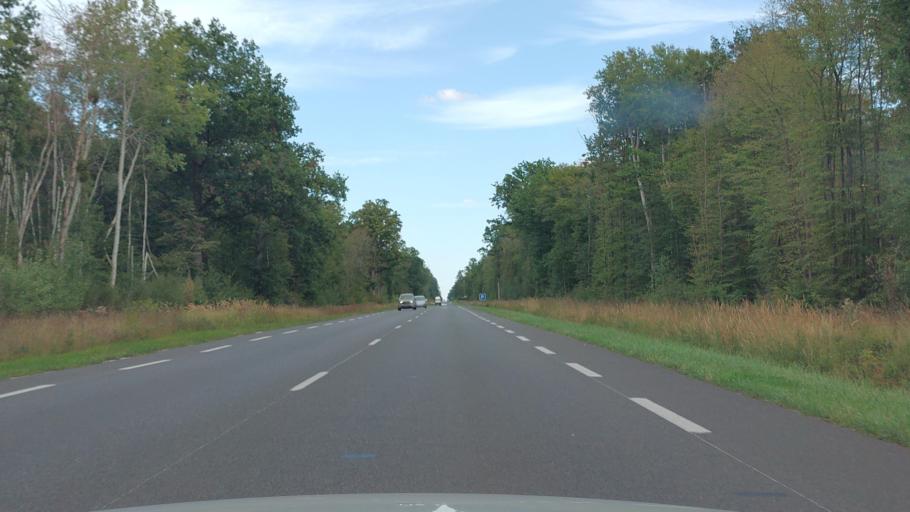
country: FR
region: Ile-de-France
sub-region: Departement de Seine-et-Marne
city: Le Chatelet-en-Brie
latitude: 48.5437
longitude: 2.8281
